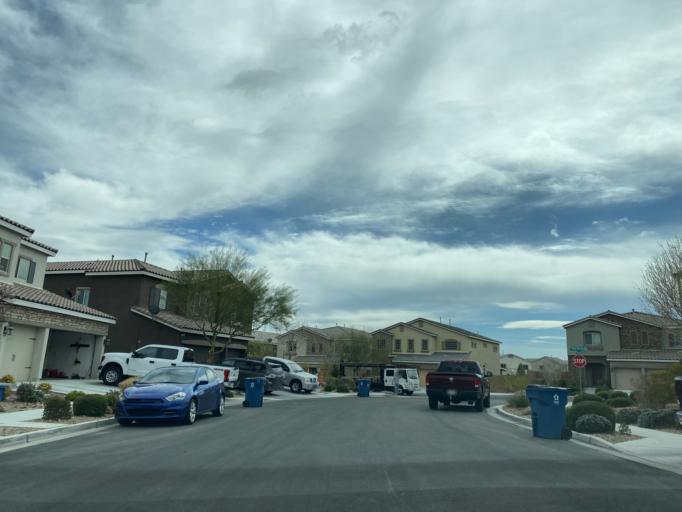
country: US
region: Nevada
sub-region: Clark County
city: Summerlin South
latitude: 36.3076
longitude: -115.2970
